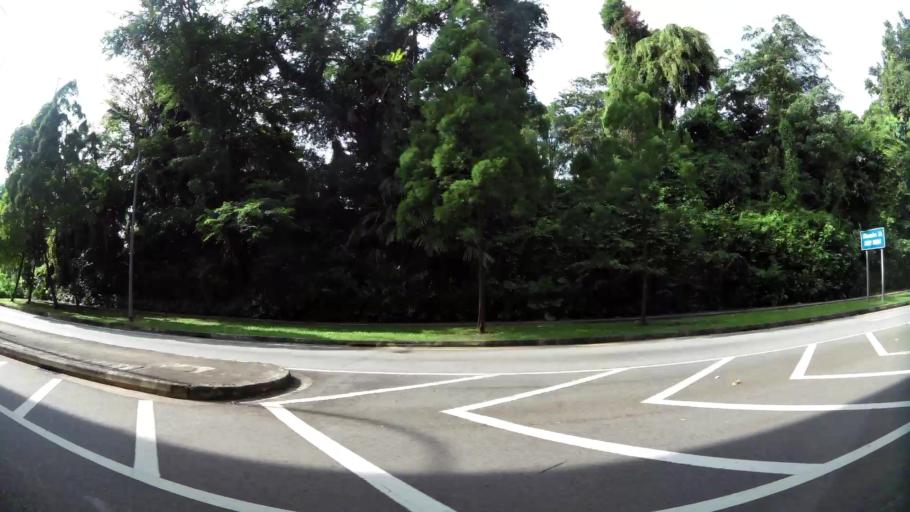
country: SG
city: Singapore
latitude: 1.2719
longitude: 103.8054
